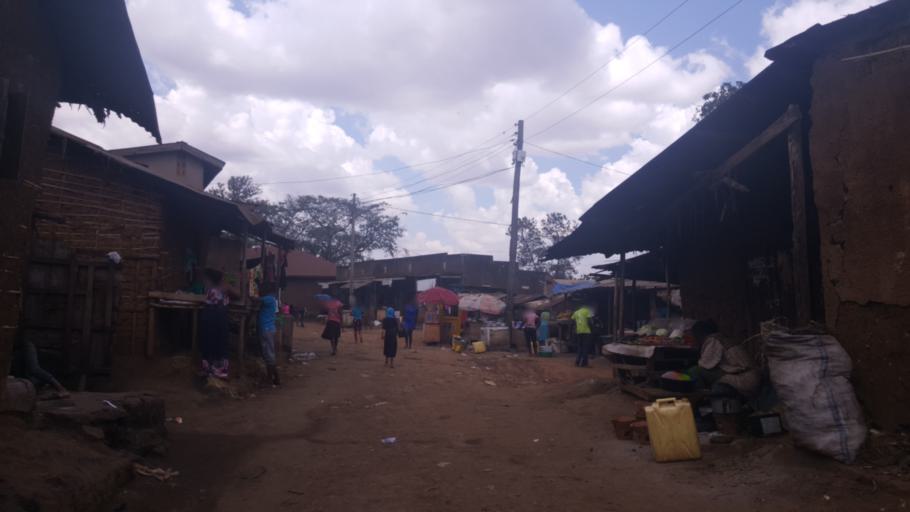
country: UG
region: Central Region
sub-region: Kampala District
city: Kampala
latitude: 0.3041
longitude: 32.5802
